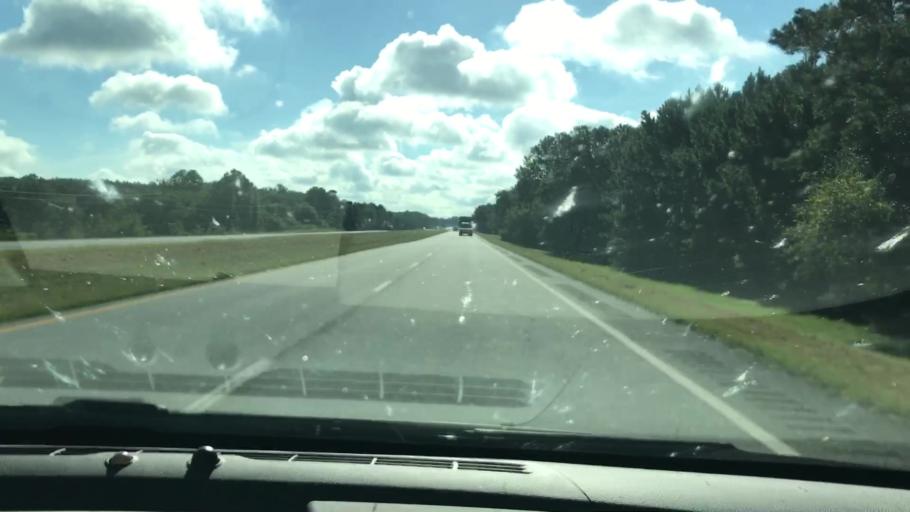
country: US
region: Georgia
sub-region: Worth County
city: Sylvester
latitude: 31.5540
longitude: -83.9861
